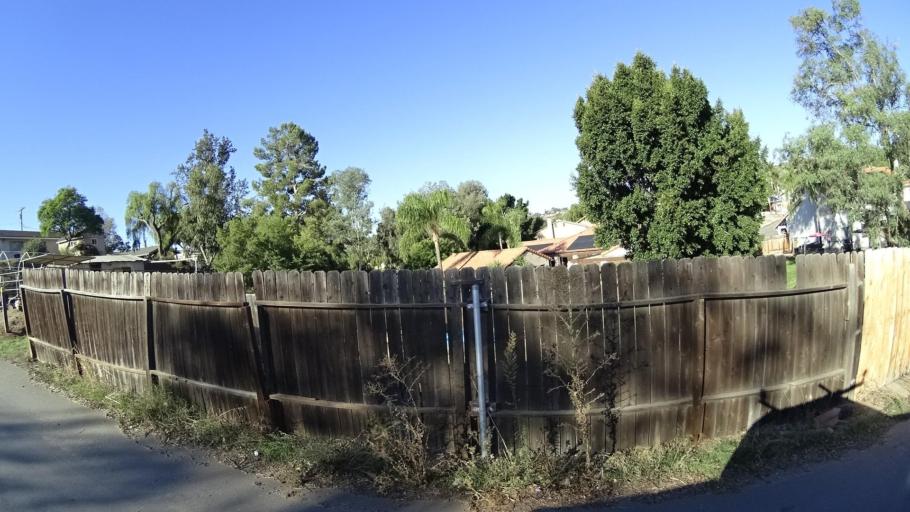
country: US
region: California
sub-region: San Diego County
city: Bonita
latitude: 32.6826
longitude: -117.0218
